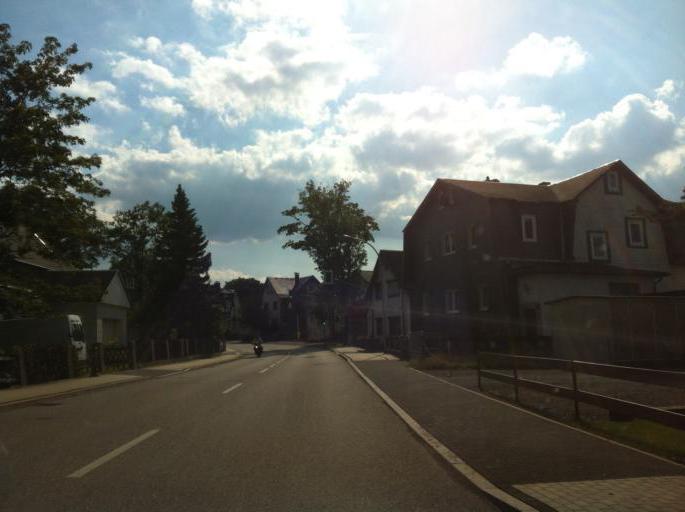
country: DE
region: Thuringia
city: Neuhaus am Rennweg
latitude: 50.5137
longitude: 11.1411
